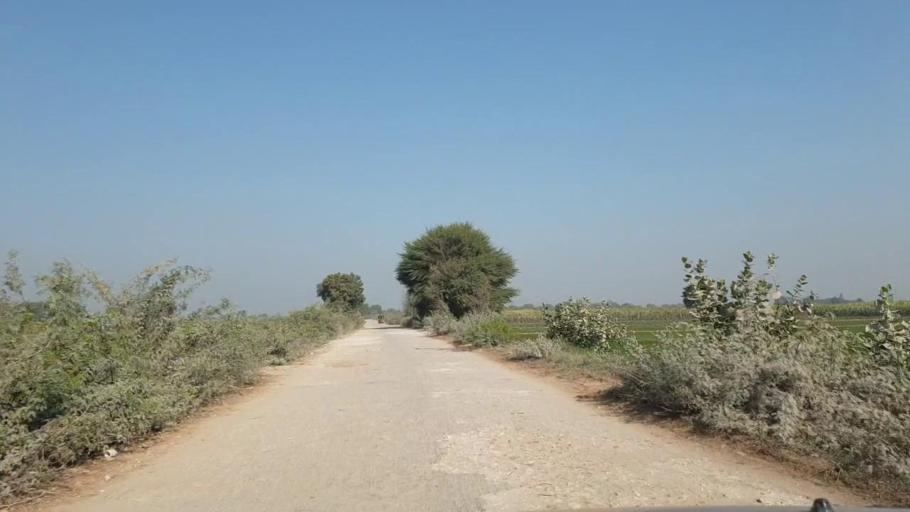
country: PK
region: Sindh
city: Tando Allahyar
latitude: 25.5635
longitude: 68.6080
